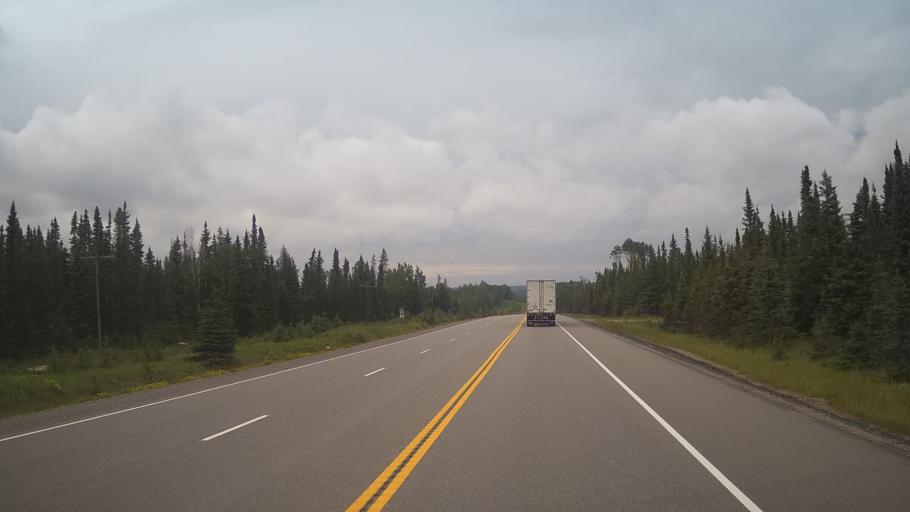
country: CA
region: Ontario
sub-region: Thunder Bay District
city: Thunder Bay
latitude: 48.7107
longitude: -89.8878
